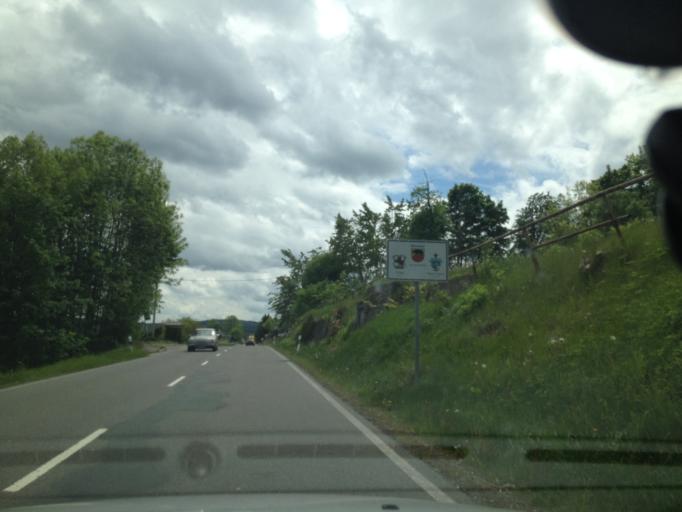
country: DE
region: Saxony
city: Barenstein
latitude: 50.5093
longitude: 13.0267
